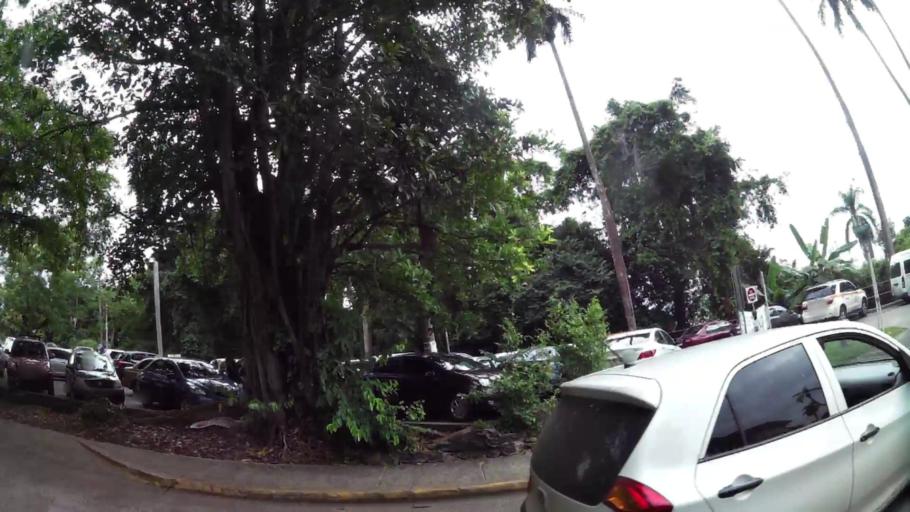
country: PA
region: Panama
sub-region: Distrito de Panama
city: Ancon
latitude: 8.9622
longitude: -79.5482
